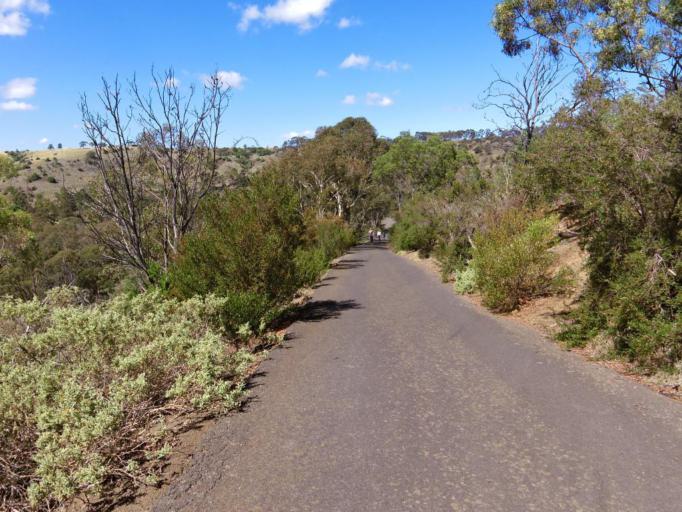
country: AU
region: Victoria
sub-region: Brimbank
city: Sydenham
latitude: -37.6656
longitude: 144.7672
